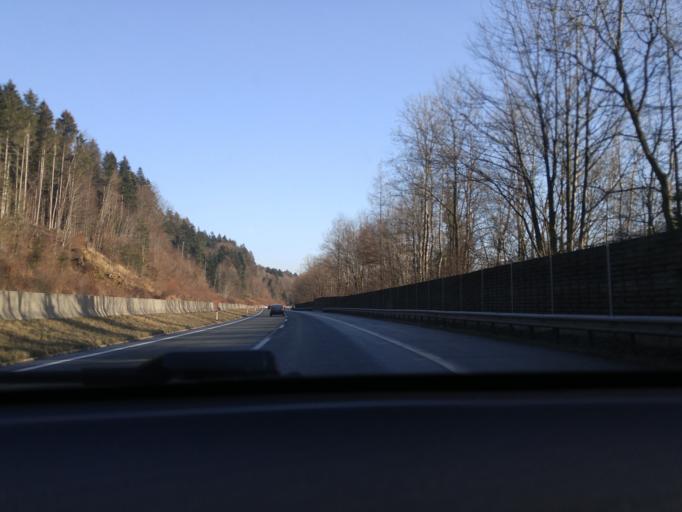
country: AT
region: Salzburg
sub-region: Politischer Bezirk Salzburg-Umgebung
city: Thalgau
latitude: 47.8472
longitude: 13.2454
